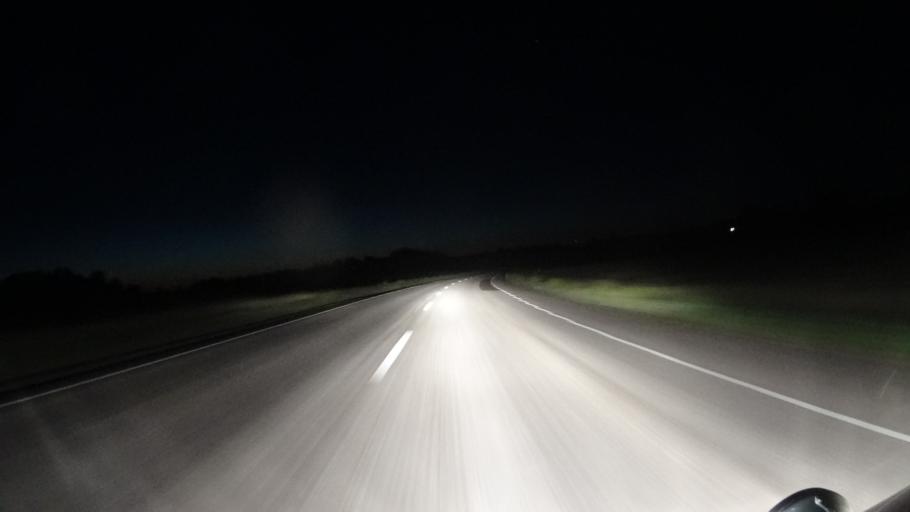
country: SE
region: OEstergoetland
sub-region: Odeshogs Kommun
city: OEdeshoeg
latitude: 58.2504
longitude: 14.7273
